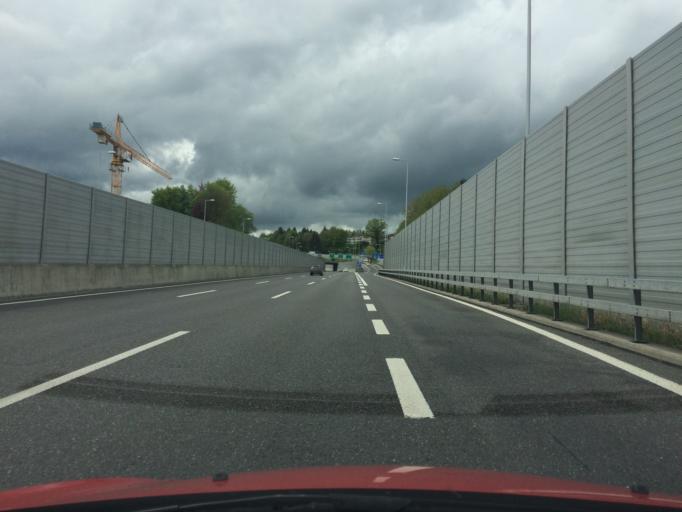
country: CH
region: Lucerne
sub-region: Hochdorf District
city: Emmen
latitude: 47.0832
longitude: 8.2775
